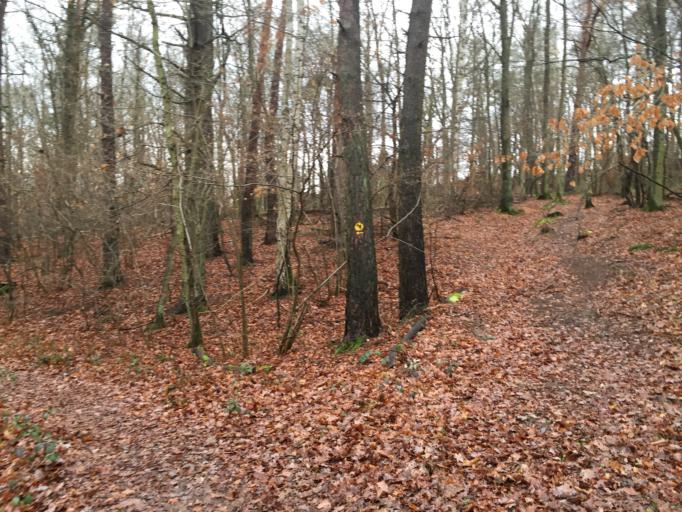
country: DE
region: Rheinland-Pfalz
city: Altleiningen
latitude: 49.5161
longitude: 8.0822
